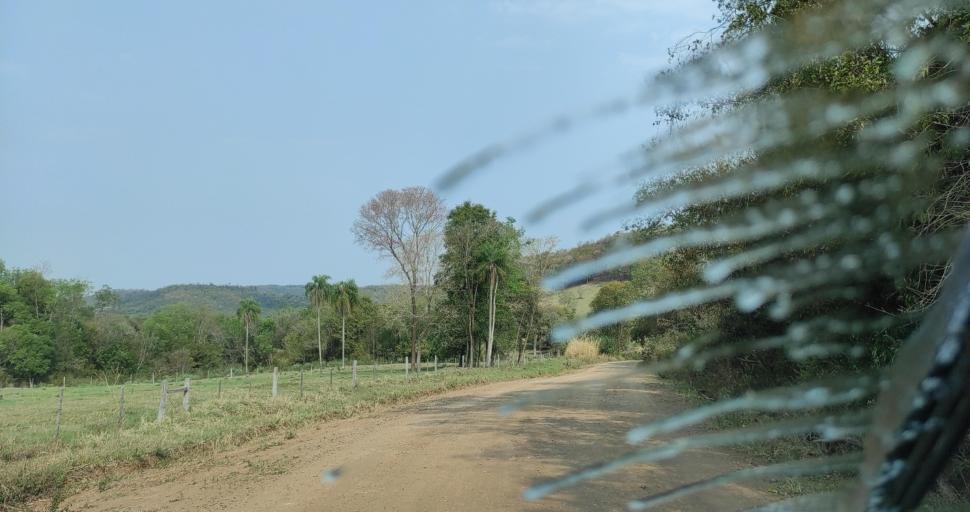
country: AR
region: Misiones
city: Cerro Cora
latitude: -27.5482
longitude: -55.5825
